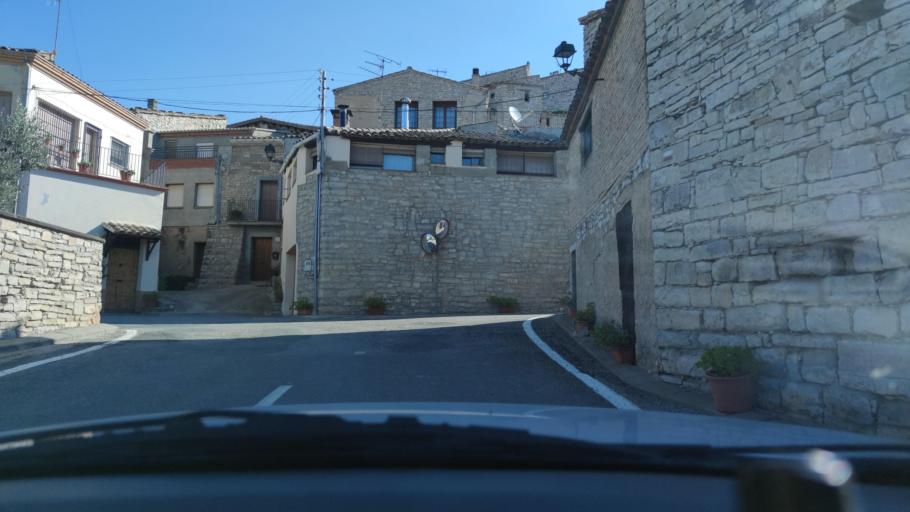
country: ES
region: Catalonia
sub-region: Provincia de Barcelona
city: Pujalt
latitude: 41.6993
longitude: 1.3628
